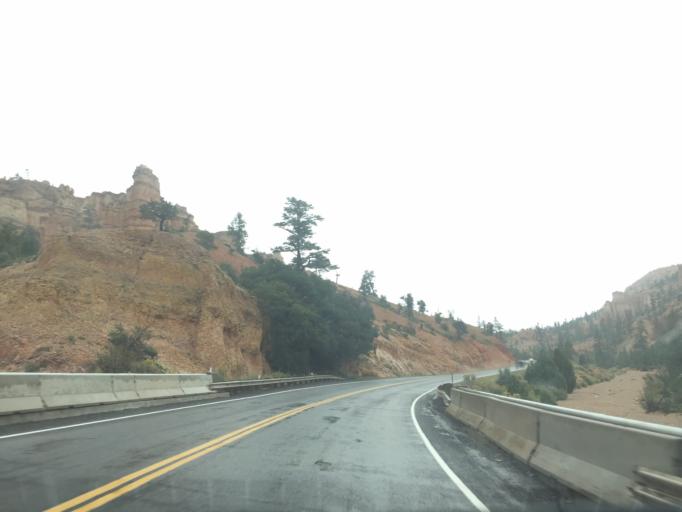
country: US
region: Utah
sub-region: Garfield County
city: Panguitch
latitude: 37.6659
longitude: -112.1101
